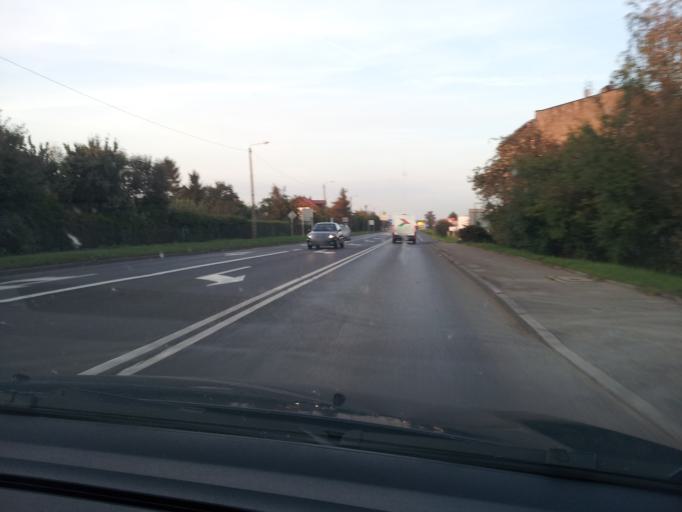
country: PL
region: Kujawsko-Pomorskie
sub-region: Powiat inowroclawski
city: Inowroclaw
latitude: 52.8053
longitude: 18.2723
